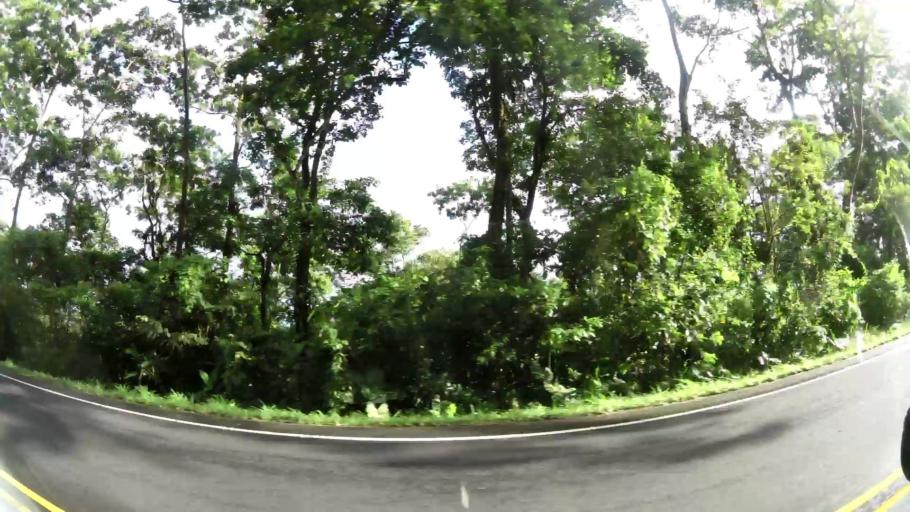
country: CR
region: Limon
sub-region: Canton de Pococi
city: Guapiles
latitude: 10.2052
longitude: -83.8223
